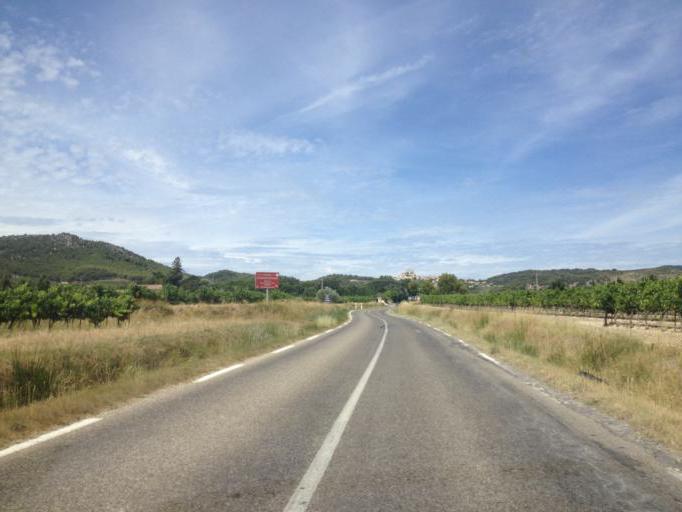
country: FR
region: Provence-Alpes-Cote d'Azur
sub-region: Departement du Vaucluse
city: Caromb
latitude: 44.1171
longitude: 5.0846
